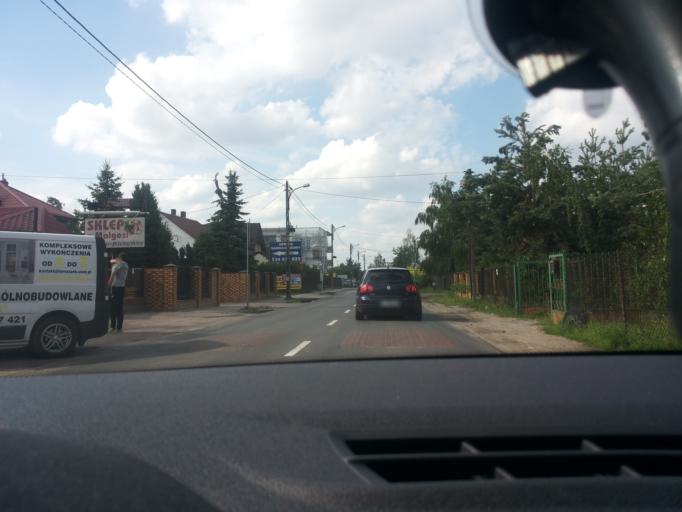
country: PL
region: Masovian Voivodeship
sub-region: Warszawa
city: Targowek
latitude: 52.3214
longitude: 21.0495
